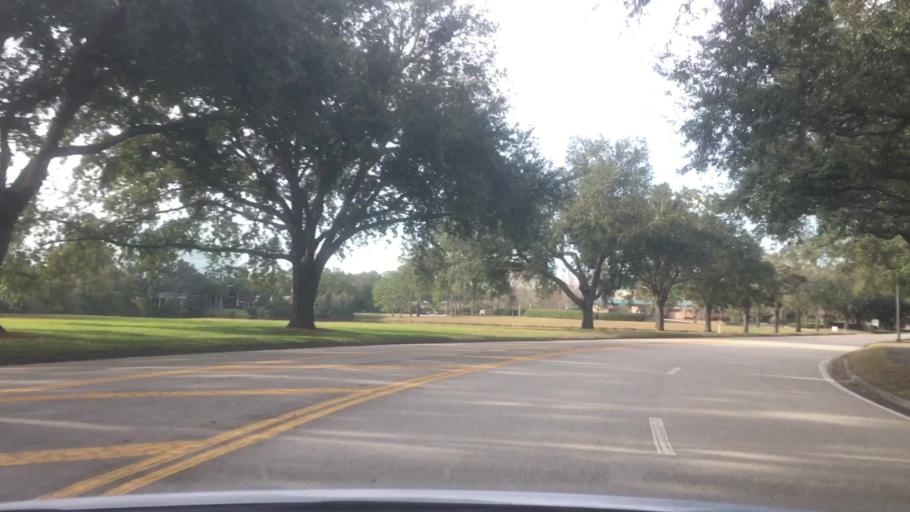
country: US
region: Florida
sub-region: Duval County
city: Jacksonville
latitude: 30.2543
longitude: -81.5851
